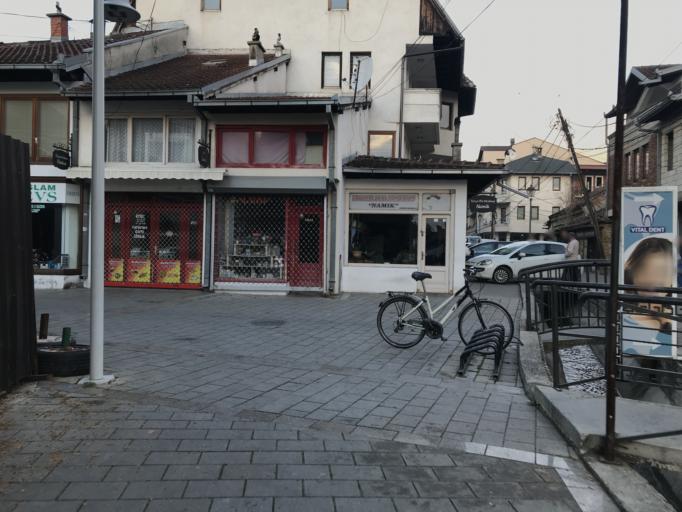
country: XK
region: Pec
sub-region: Komuna e Pejes
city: Peje
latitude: 42.6606
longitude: 20.2945
